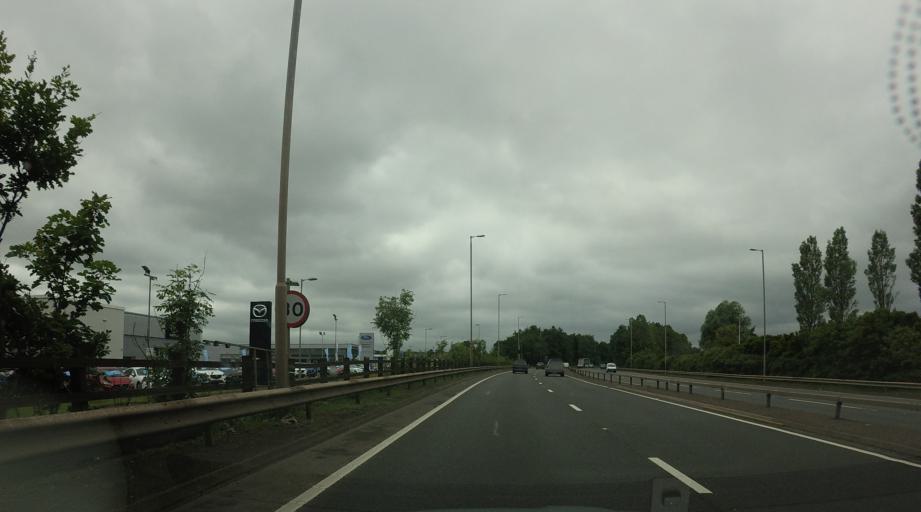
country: GB
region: Scotland
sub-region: South Lanarkshire
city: Bothwell
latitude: 55.7924
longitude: -4.0704
